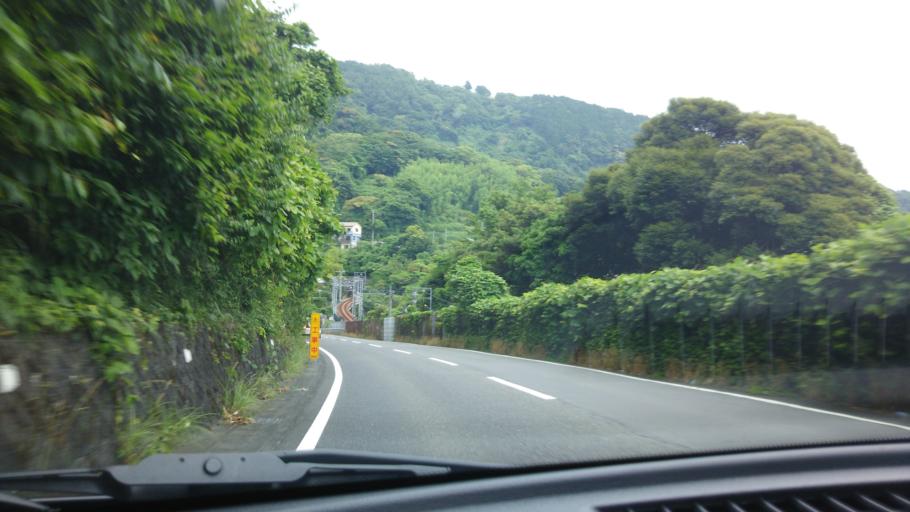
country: JP
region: Shizuoka
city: Ito
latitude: 34.8275
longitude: 139.0750
